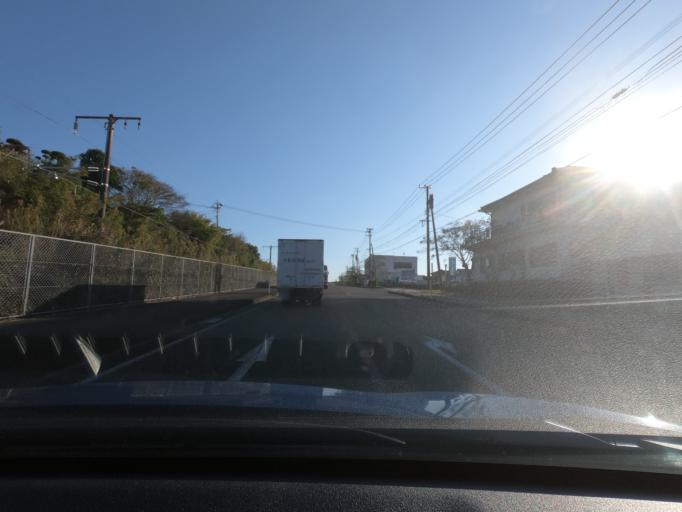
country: JP
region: Kagoshima
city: Akune
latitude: 32.0097
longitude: 130.1969
